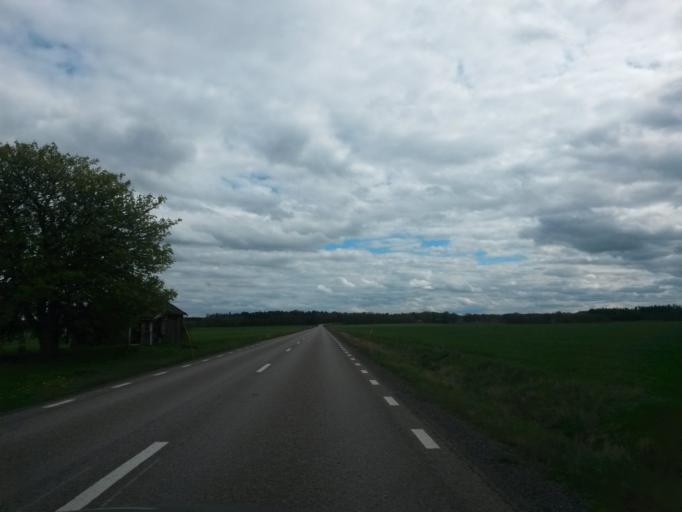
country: SE
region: Vaestra Goetaland
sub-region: Essunga Kommun
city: Nossebro
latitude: 58.2544
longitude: 12.6932
